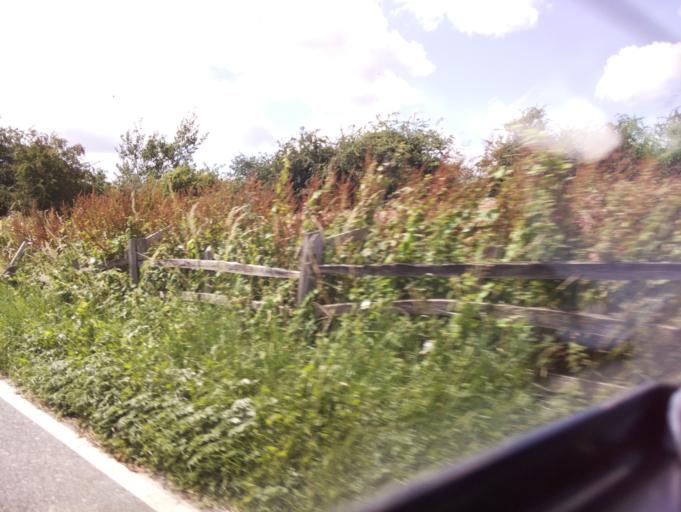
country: GB
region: England
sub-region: Nottinghamshire
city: Burton Joyce
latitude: 53.0087
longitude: -1.0268
